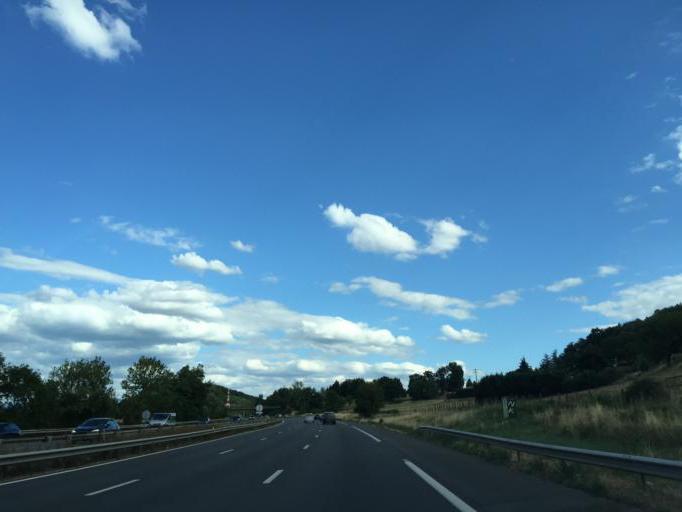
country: FR
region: Rhone-Alpes
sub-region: Departement de la Loire
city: La Fouillouse
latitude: 45.4899
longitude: 4.3209
